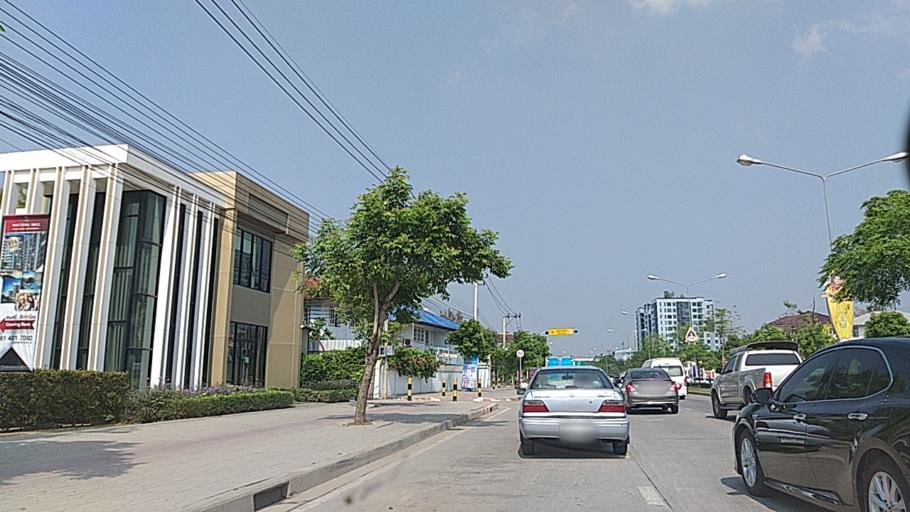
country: TH
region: Bangkok
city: Bang Khen
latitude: 13.8885
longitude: 100.6105
